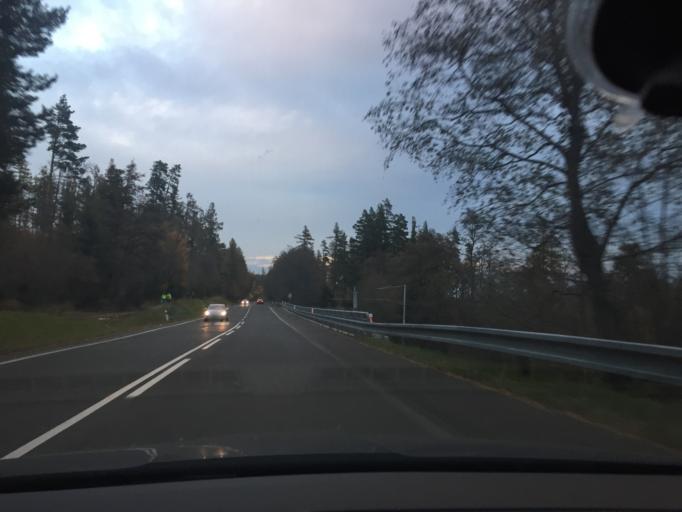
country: SK
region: Presovsky
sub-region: Okres Poprad
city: Vysoke Tatry
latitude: 49.1456
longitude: 20.2477
